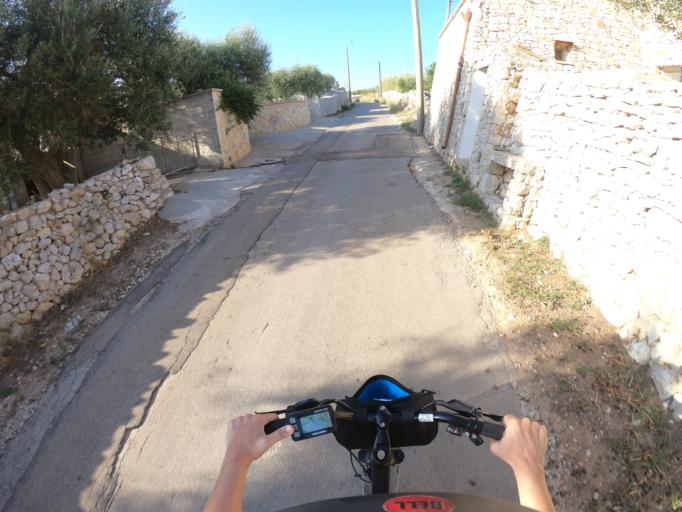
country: IT
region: Apulia
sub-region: Provincia di Lecce
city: Castrignano del Capo
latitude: 39.8281
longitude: 18.3587
